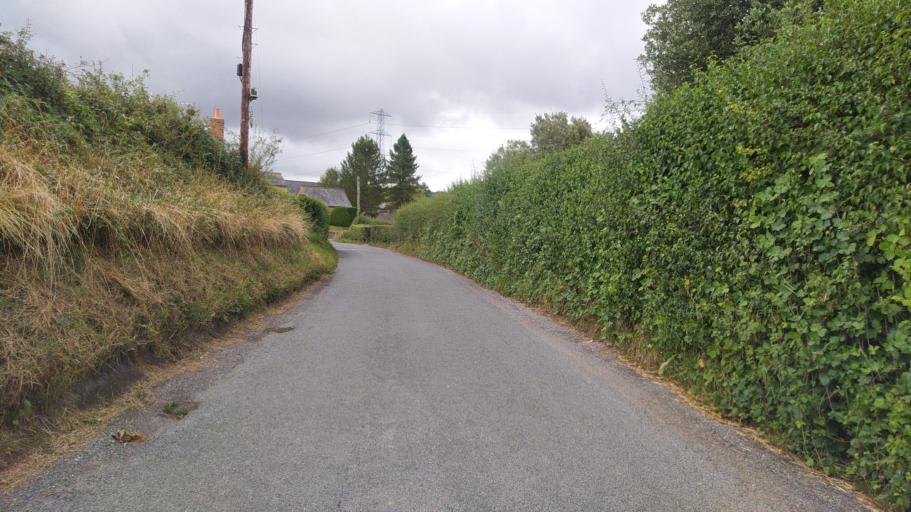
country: GB
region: England
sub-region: Hampshire
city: Petersfield
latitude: 50.9861
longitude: -1.0156
